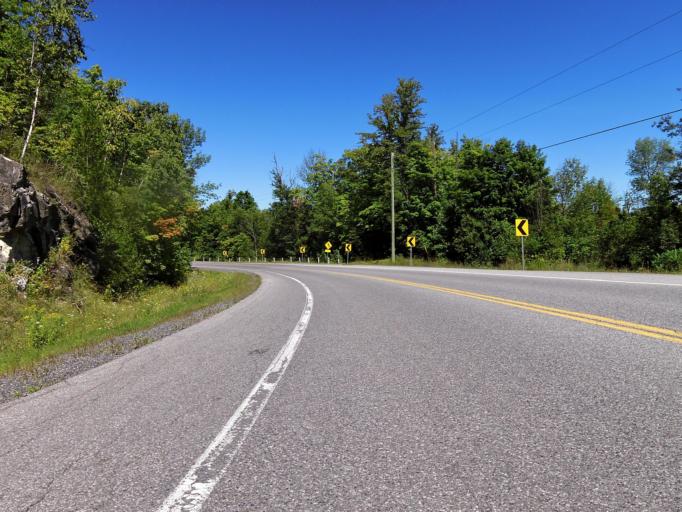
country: CA
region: Ontario
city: Arnprior
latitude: 45.1577
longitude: -76.5180
